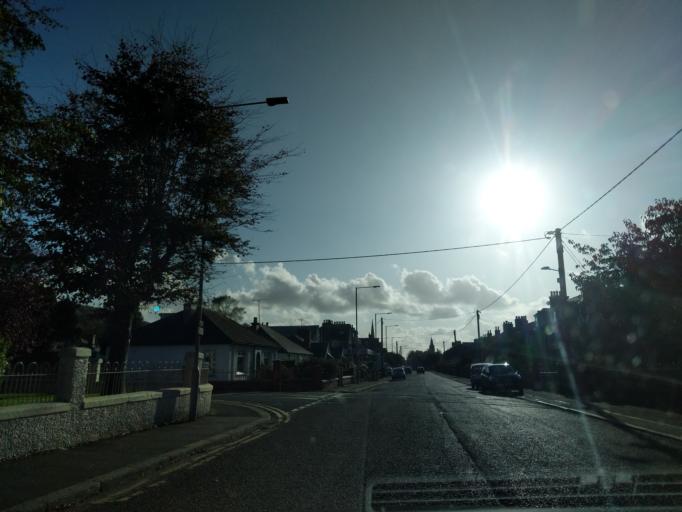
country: GB
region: Scotland
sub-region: Dumfries and Galloway
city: Kirkcudbright
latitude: 54.8412
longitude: -4.0439
